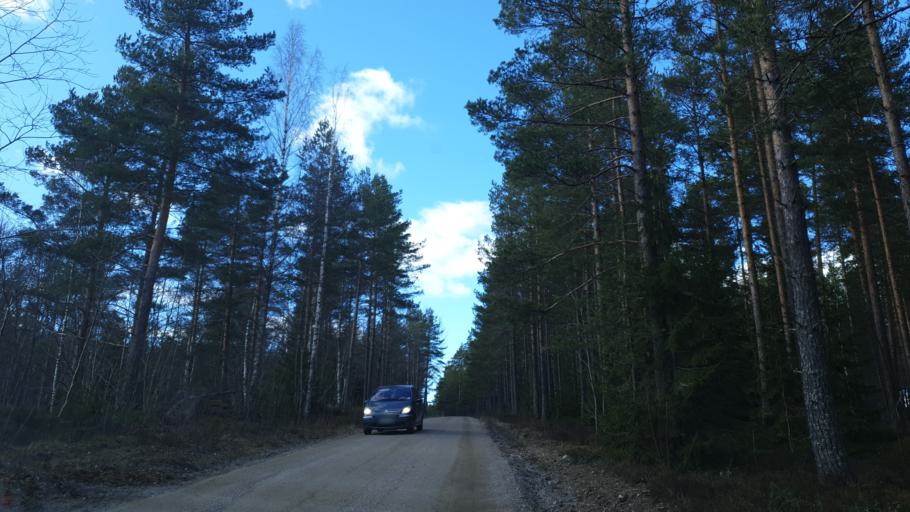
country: SE
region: OErebro
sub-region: Orebro Kommun
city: Garphyttan
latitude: 59.3529
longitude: 14.9851
